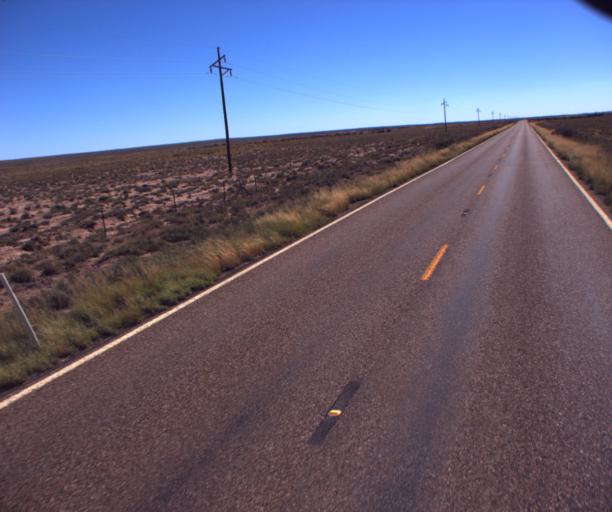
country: US
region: Arizona
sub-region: Navajo County
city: Holbrook
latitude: 35.0933
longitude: -110.0969
